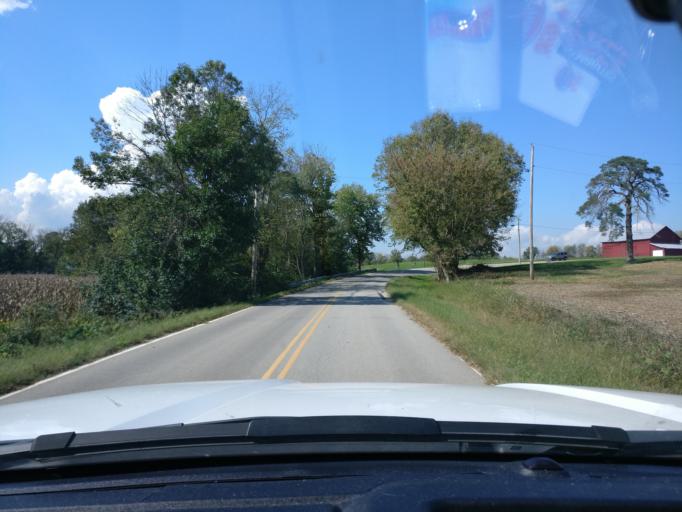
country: US
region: Ohio
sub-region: Warren County
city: Waynesville
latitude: 39.4905
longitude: -84.0006
